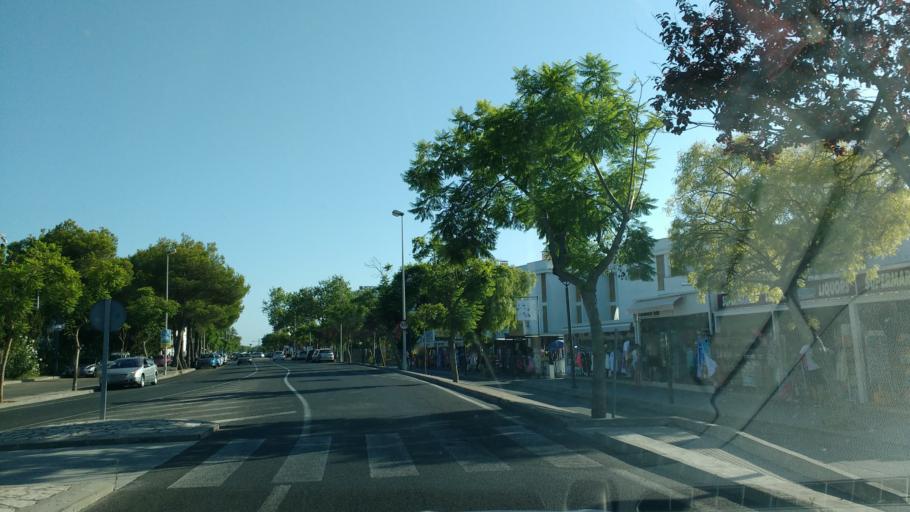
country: ES
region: Balearic Islands
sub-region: Illes Balears
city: Port d'Alcudia
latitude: 39.8352
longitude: 3.1182
